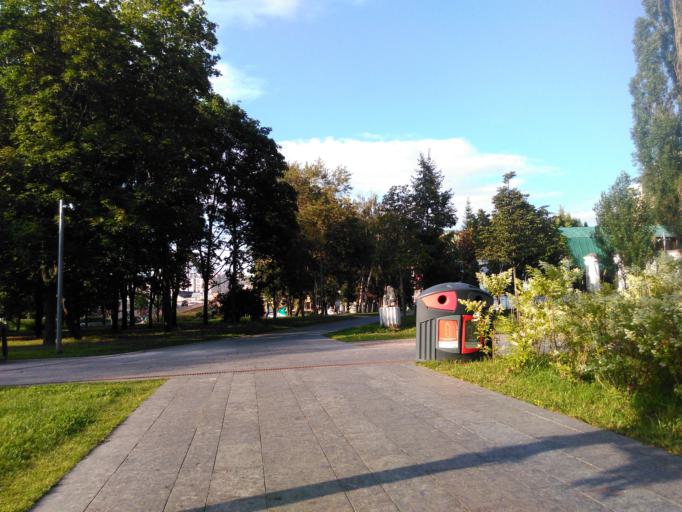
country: RU
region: Moscow
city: Moscow
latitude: 55.7377
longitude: 37.6099
